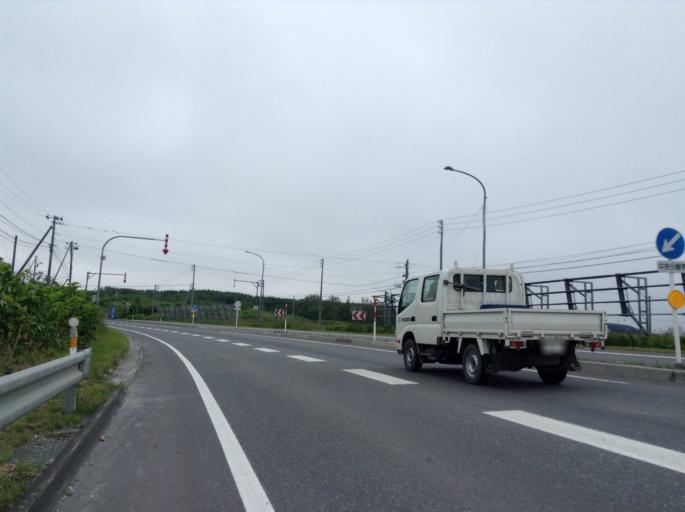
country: JP
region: Hokkaido
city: Wakkanai
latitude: 45.3761
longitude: 141.7124
